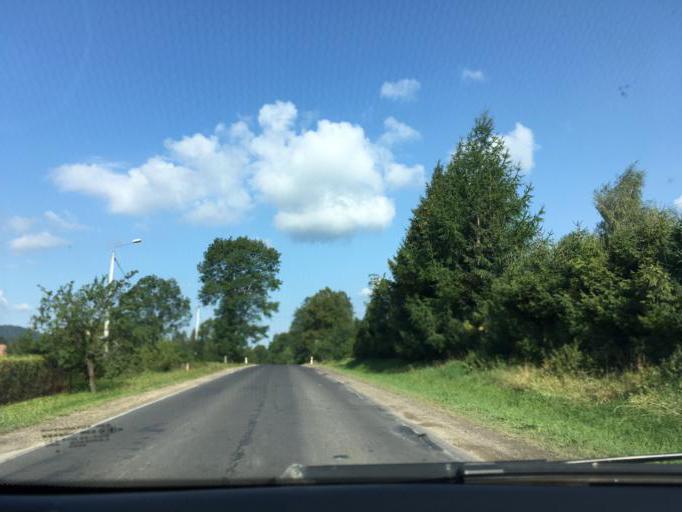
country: PL
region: Subcarpathian Voivodeship
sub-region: Powiat bieszczadzki
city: Czarna
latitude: 49.3632
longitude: 22.6664
